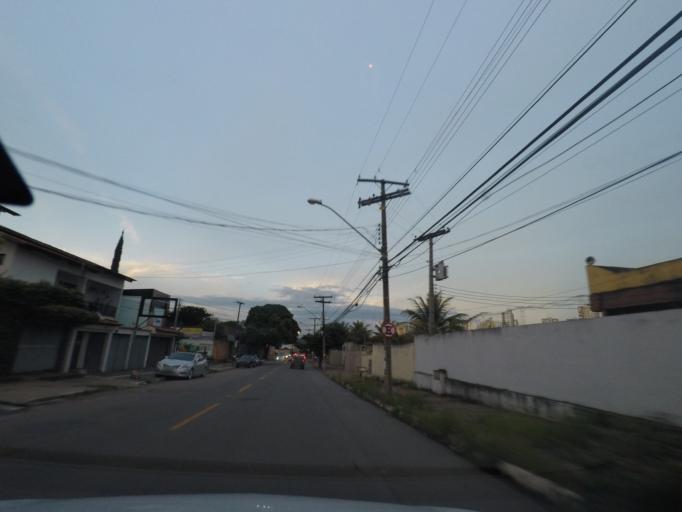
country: BR
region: Goias
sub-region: Goiania
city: Goiania
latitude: -16.7004
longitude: -49.2504
